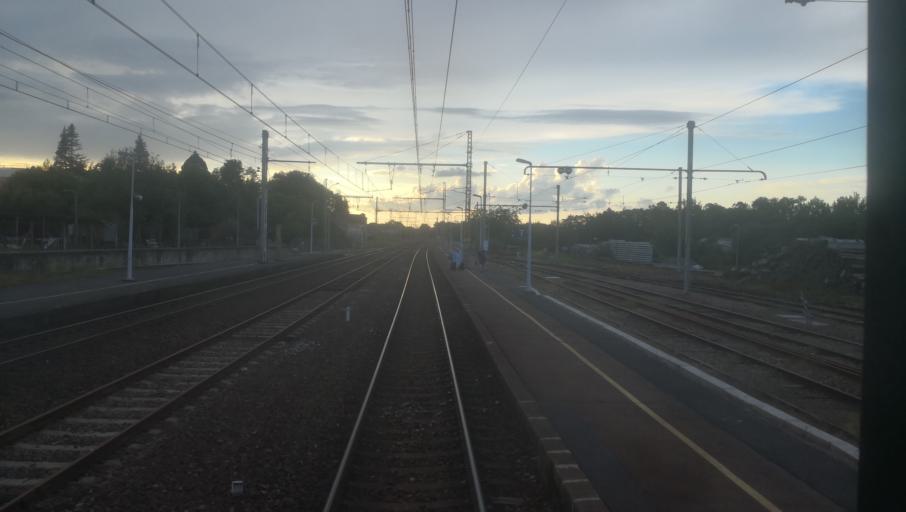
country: FR
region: Limousin
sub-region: Departement de la Creuse
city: La Souterraine
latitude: 46.2418
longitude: 1.4908
